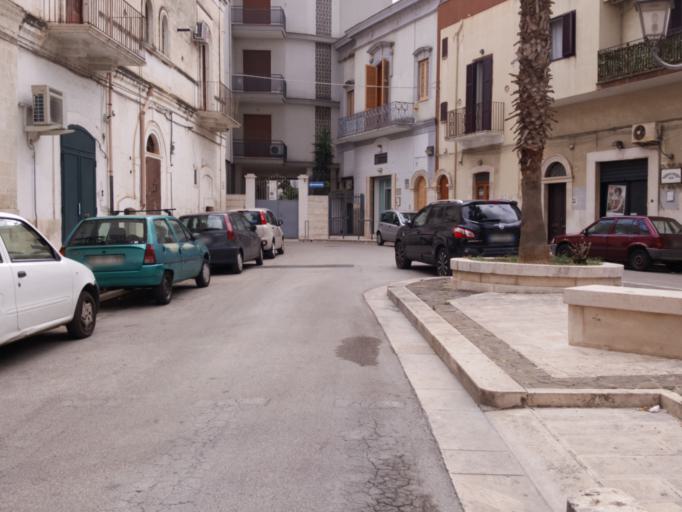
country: IT
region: Apulia
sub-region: Provincia di Bari
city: Triggiano
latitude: 41.0653
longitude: 16.9233
